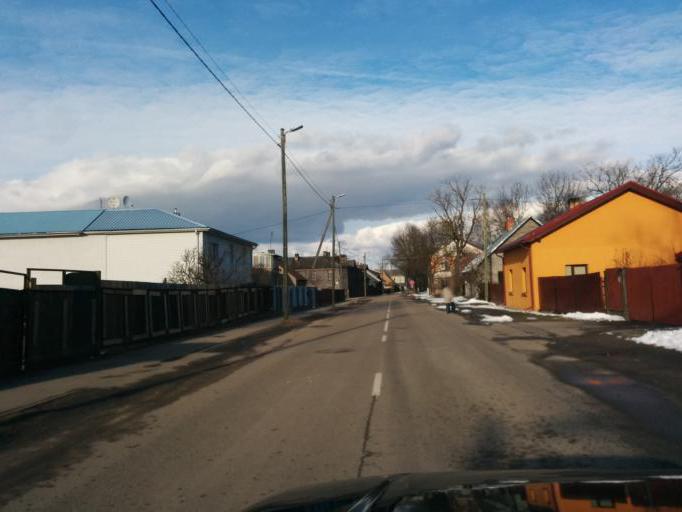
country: LV
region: Jelgava
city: Jelgava
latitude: 56.6564
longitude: 23.7138
